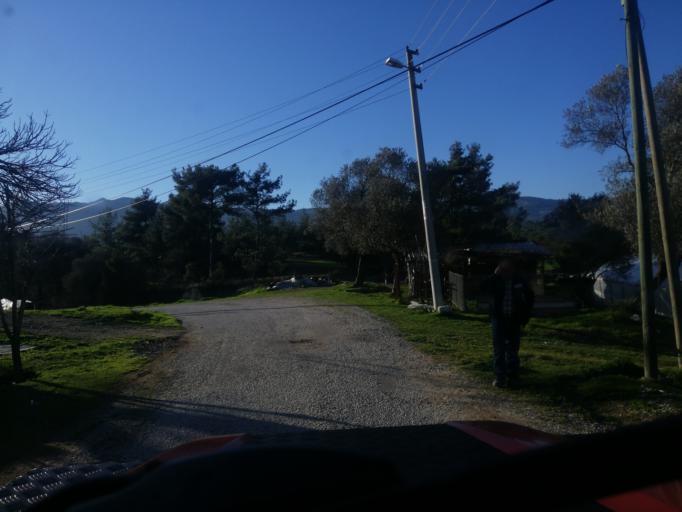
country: TR
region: Antalya
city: Kas
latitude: 36.2898
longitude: 29.7113
